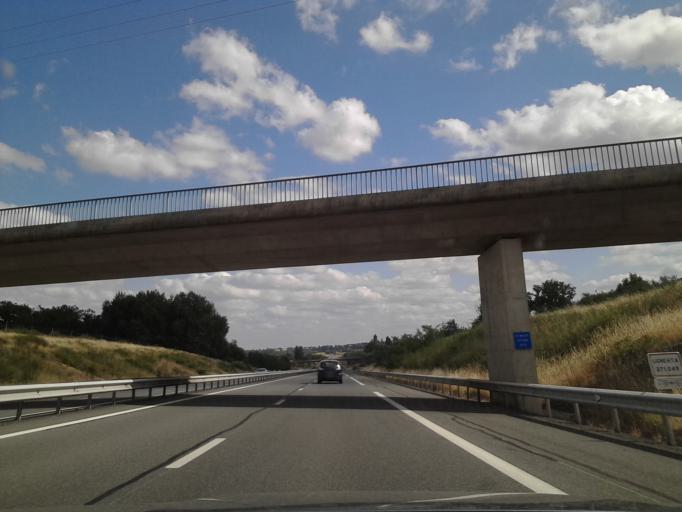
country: FR
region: Auvergne
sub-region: Departement de l'Allier
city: Vallon-en-Sully
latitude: 46.5579
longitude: 2.5458
